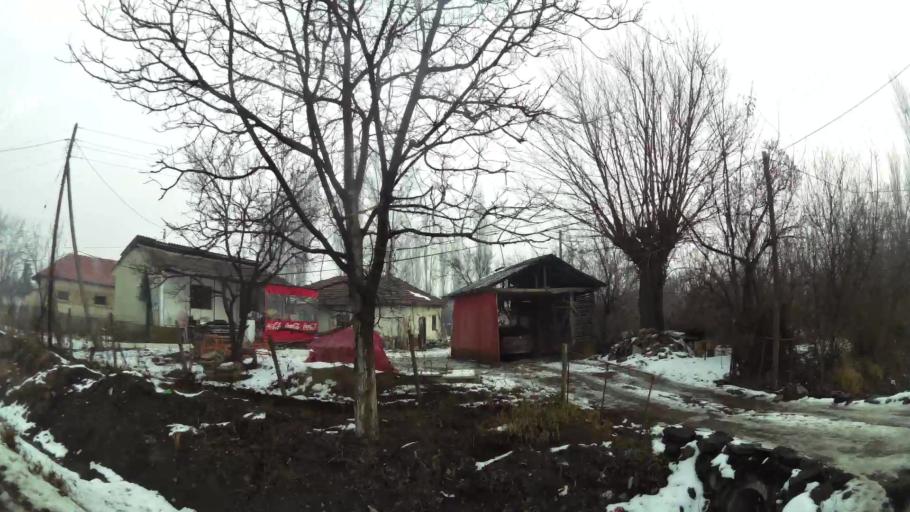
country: MK
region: Ilinden
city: Idrizovo
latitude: 41.9637
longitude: 21.5724
